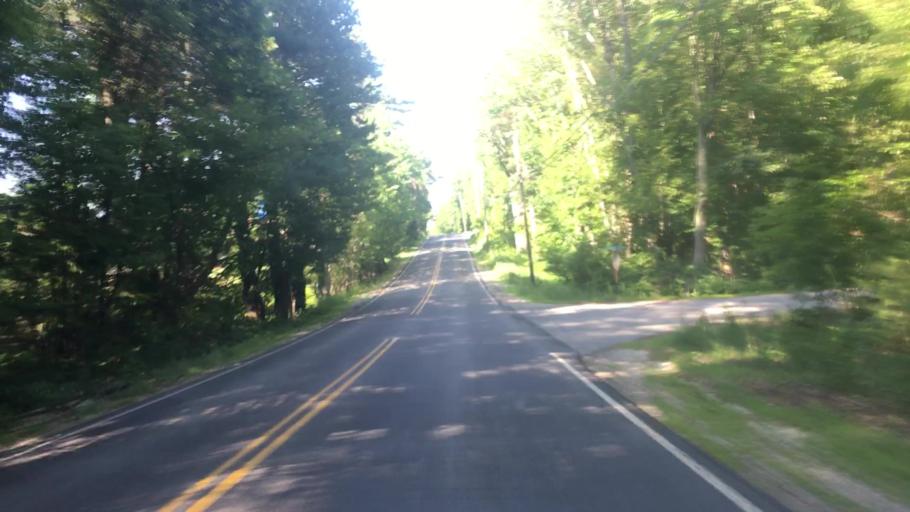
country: US
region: Maine
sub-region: York County
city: Buxton
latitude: 43.7246
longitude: -70.5622
